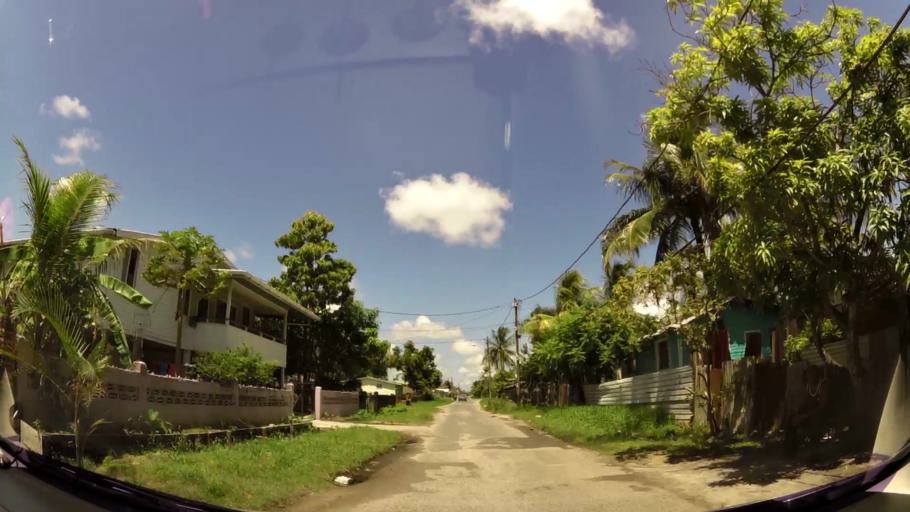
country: GY
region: Demerara-Mahaica
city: Georgetown
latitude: 6.7922
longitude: -58.1454
